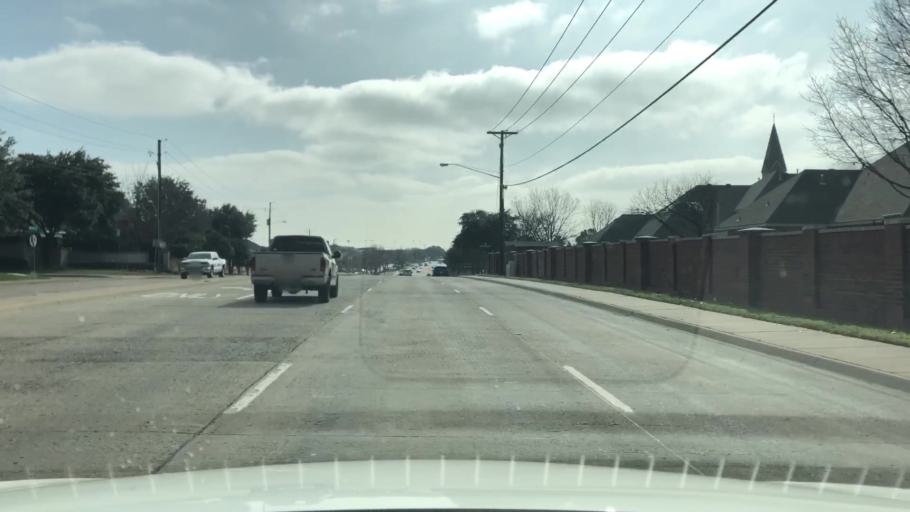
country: US
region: Texas
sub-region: Dallas County
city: Addison
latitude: 32.9923
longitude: -96.8551
